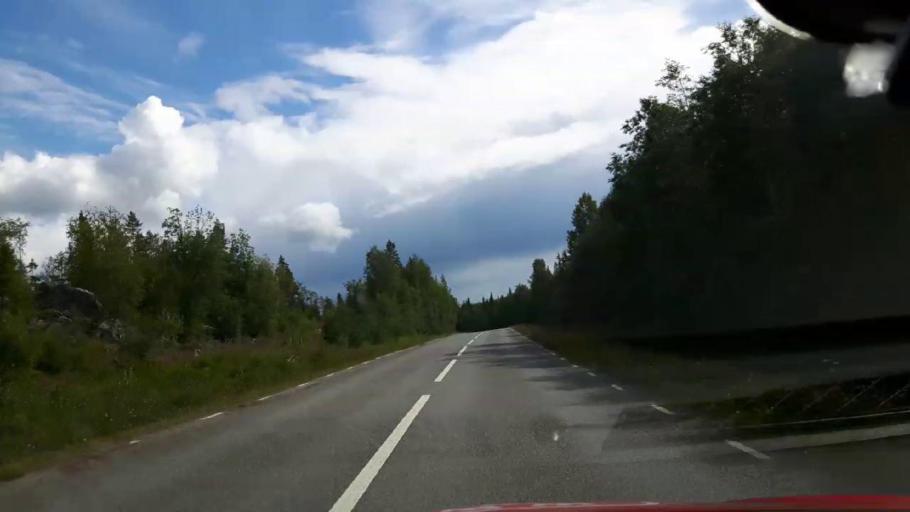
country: SE
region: Jaemtland
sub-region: Stroemsunds Kommun
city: Stroemsund
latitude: 64.3439
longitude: 15.1070
